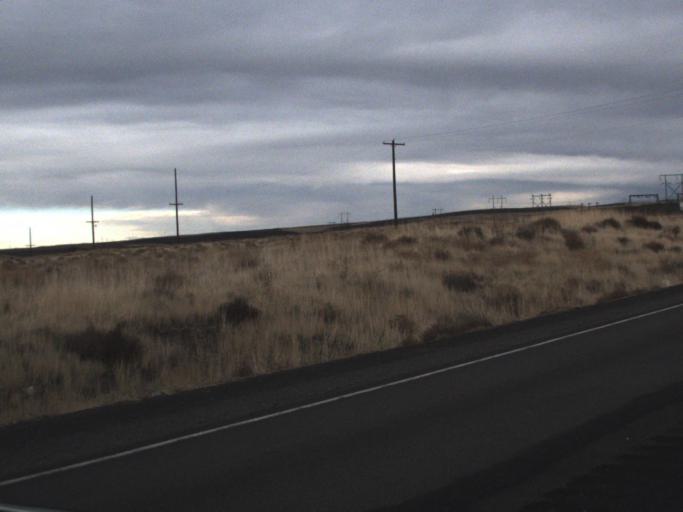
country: US
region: Washington
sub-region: Benton County
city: Finley
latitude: 46.0611
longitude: -118.8487
